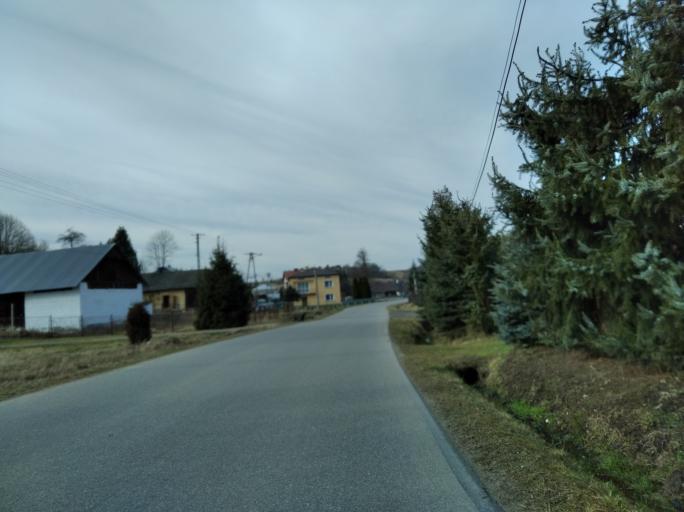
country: PL
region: Subcarpathian Voivodeship
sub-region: Powiat brzozowski
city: Gorki
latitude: 49.6417
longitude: 22.0524
